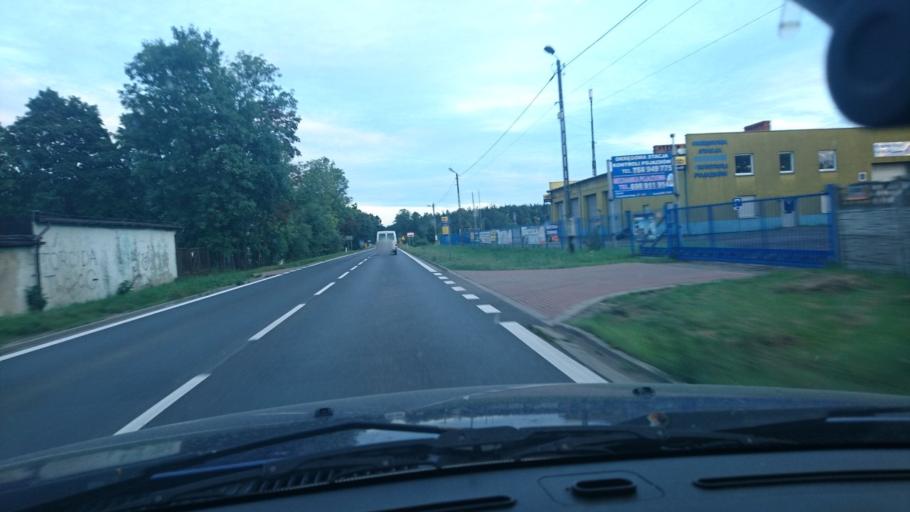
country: PL
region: Silesian Voivodeship
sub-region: Powiat tarnogorski
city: Tworog
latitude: 50.5277
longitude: 18.7177
